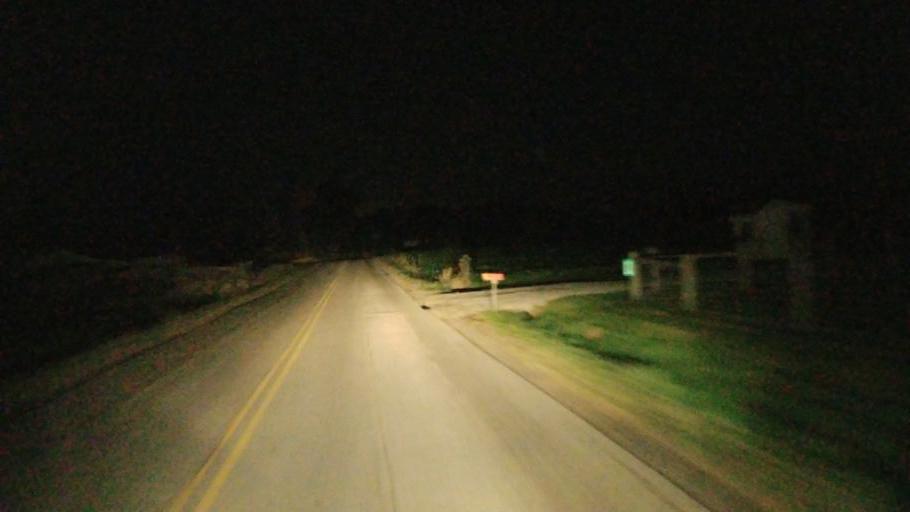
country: US
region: Ohio
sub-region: Wayne County
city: Apple Creek
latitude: 40.6947
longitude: -81.7459
